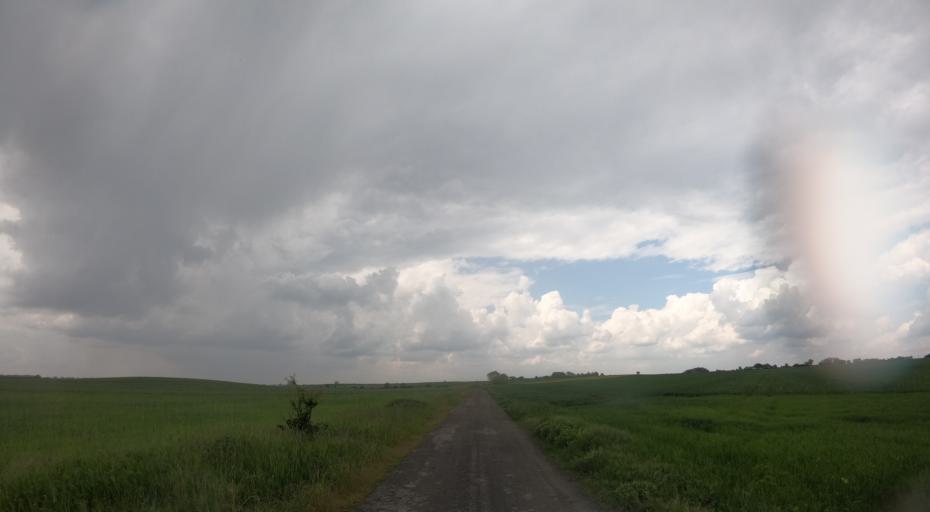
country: PL
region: West Pomeranian Voivodeship
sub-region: Powiat pyrzycki
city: Bielice
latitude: 53.2424
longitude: 14.7224
